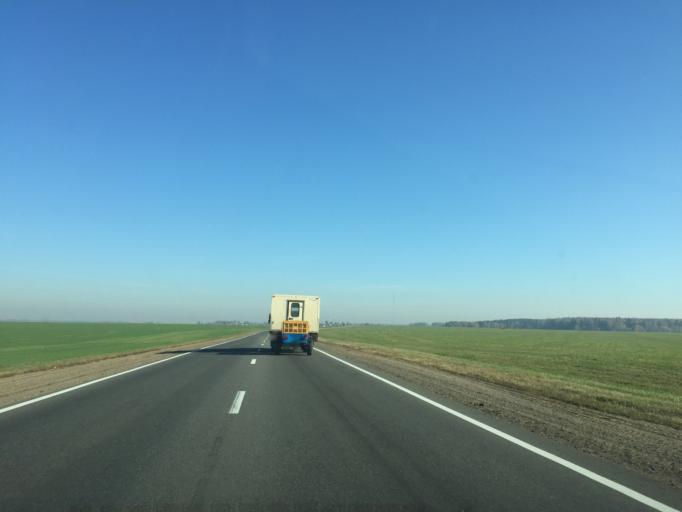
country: BY
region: Mogilev
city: Mahilyow
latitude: 53.9628
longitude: 30.2456
